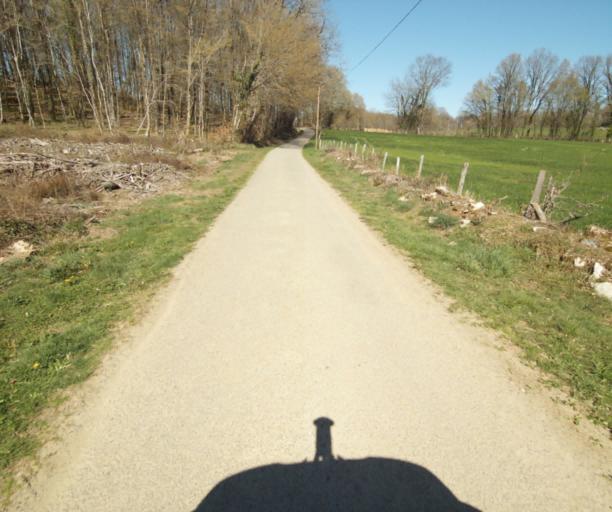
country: FR
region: Limousin
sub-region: Departement de la Correze
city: Chameyrat
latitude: 45.2507
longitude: 1.7062
